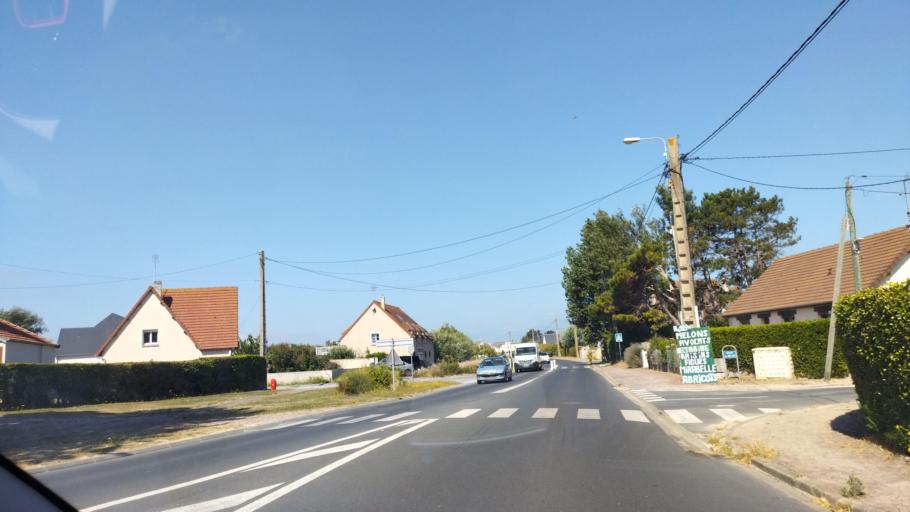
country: FR
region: Lower Normandy
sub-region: Departement du Calvados
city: Bernieres-sur-Mer
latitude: 49.3336
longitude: -0.4076
